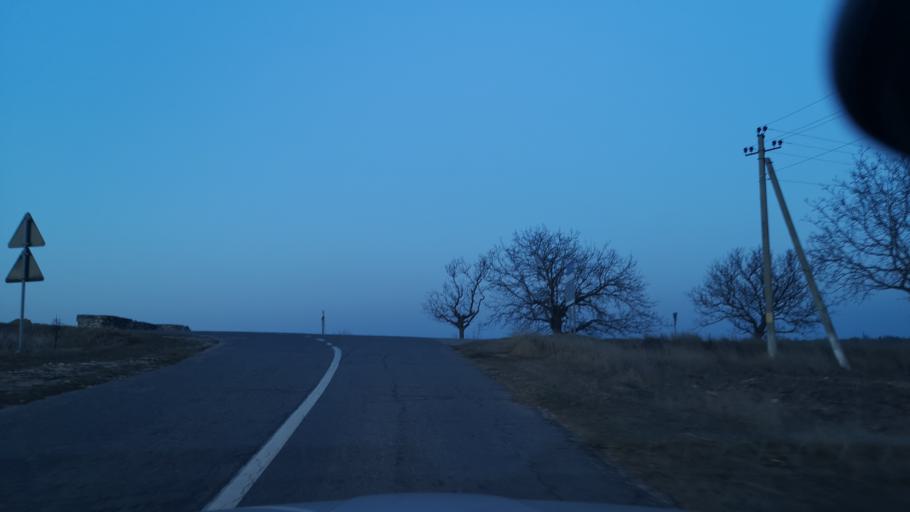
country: MD
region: Telenesti
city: Cocieri
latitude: 47.3088
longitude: 28.9741
